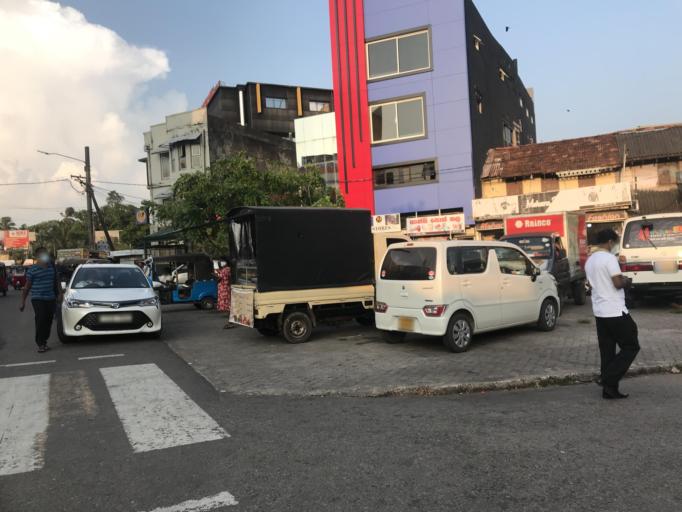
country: LK
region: Western
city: Gampaha
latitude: 7.0930
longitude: 79.9937
